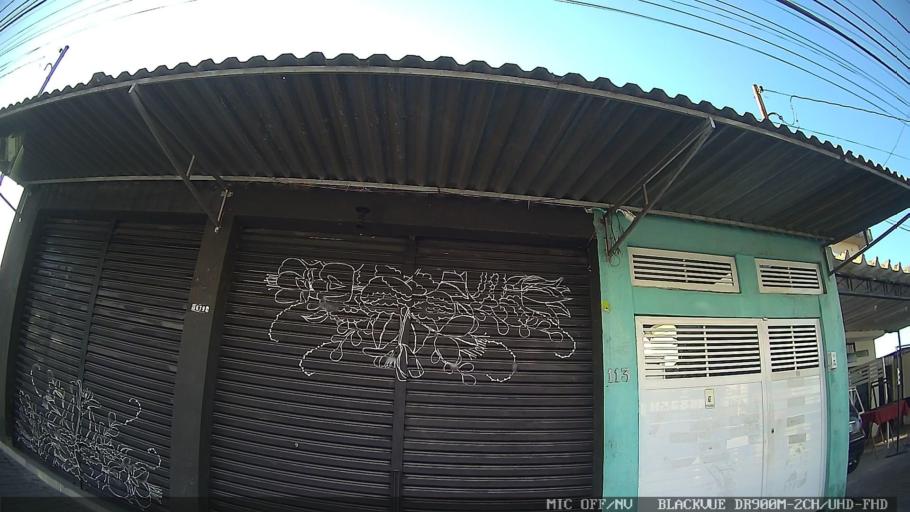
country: BR
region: Sao Paulo
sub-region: Santos
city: Santos
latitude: -23.9607
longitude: -46.2942
